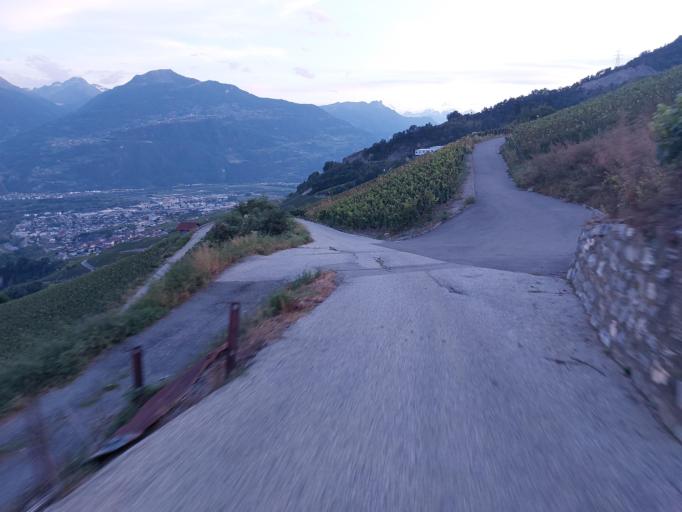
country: CH
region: Valais
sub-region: Conthey District
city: Conthey
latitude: 46.2526
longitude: 7.3068
